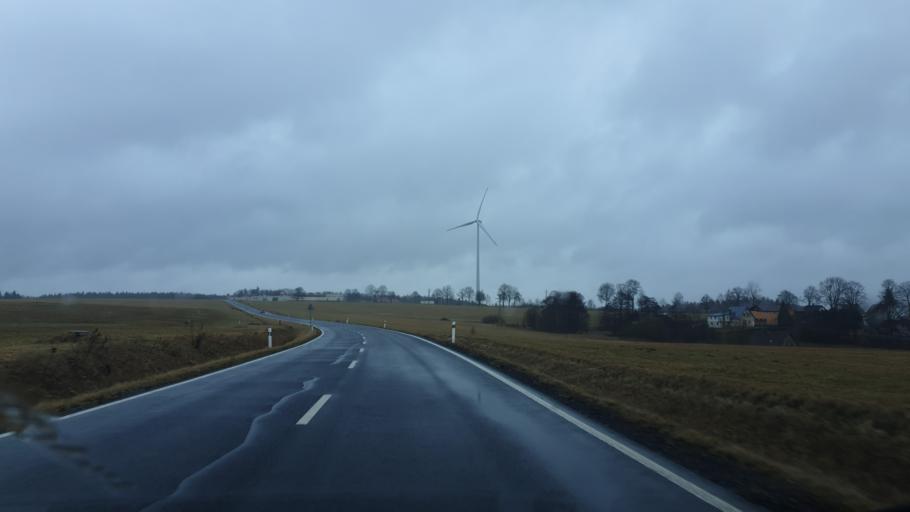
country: CZ
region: Karlovarsky
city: Hranice
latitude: 50.3102
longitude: 12.1662
